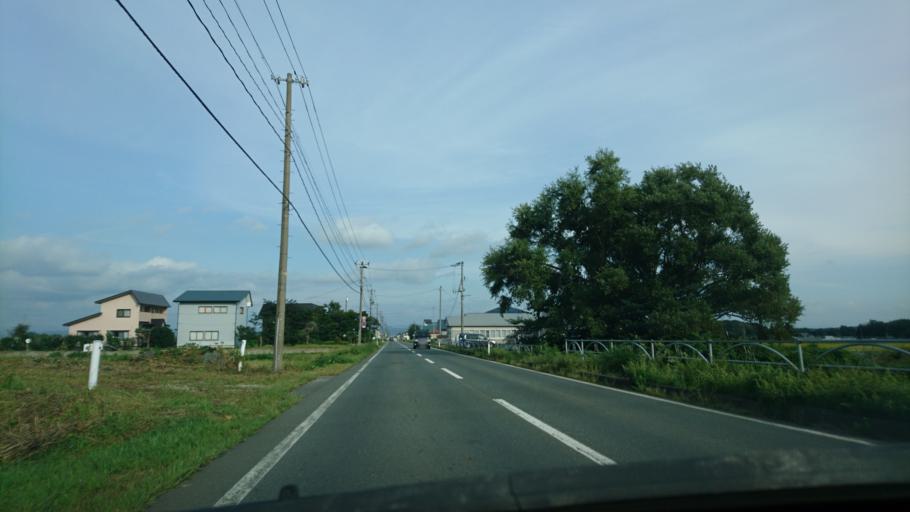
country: JP
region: Iwate
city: Kitakami
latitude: 39.3055
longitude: 141.0085
